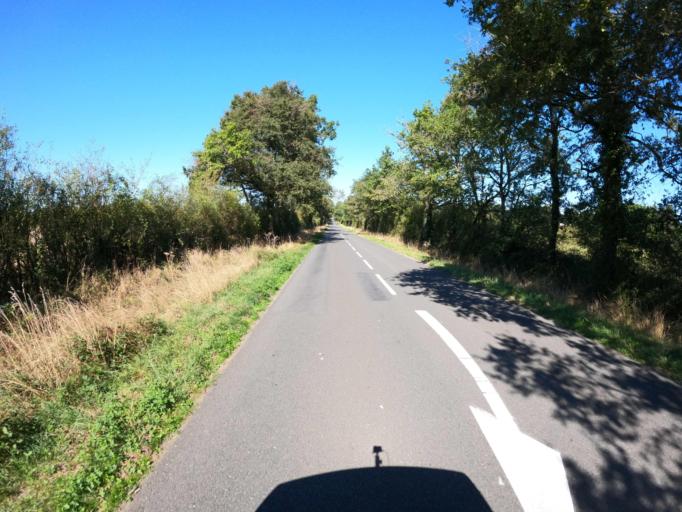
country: FR
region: Poitou-Charentes
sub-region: Departement de la Vienne
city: Lathus-Saint-Remy
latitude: 46.3253
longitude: 0.9680
